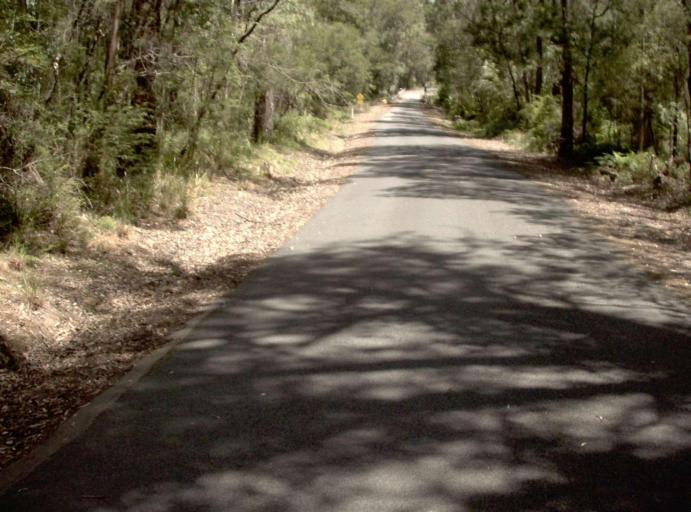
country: AU
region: New South Wales
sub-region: Bombala
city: Bombala
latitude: -37.4370
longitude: 148.9844
